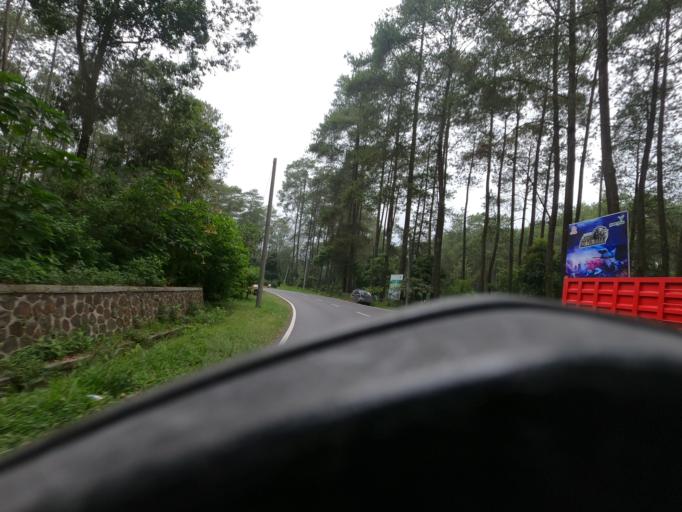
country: ID
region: West Java
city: Lembang
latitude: -6.7814
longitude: 107.6471
